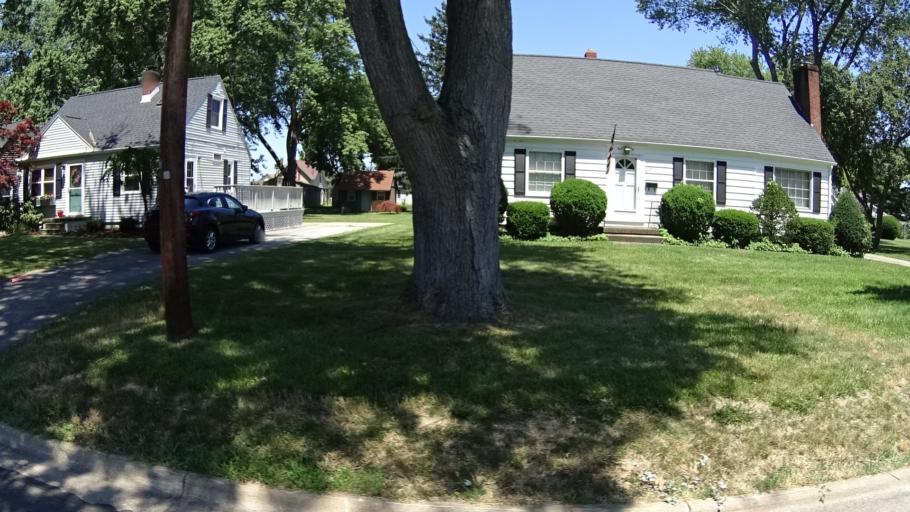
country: US
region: Ohio
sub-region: Erie County
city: Huron
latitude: 41.3935
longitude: -82.5663
